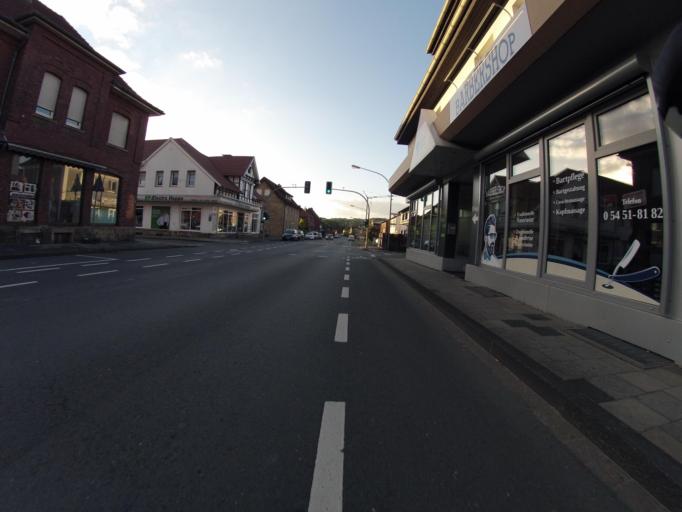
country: DE
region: North Rhine-Westphalia
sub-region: Regierungsbezirk Munster
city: Tecklenburg
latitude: 52.2646
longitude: 7.7891
